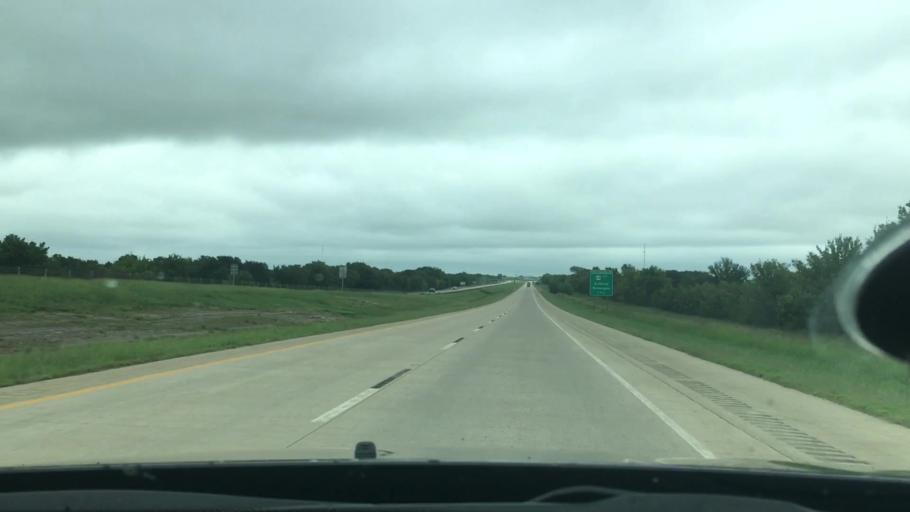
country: US
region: Oklahoma
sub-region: McIntosh County
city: Checotah
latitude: 35.4572
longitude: -95.5715
